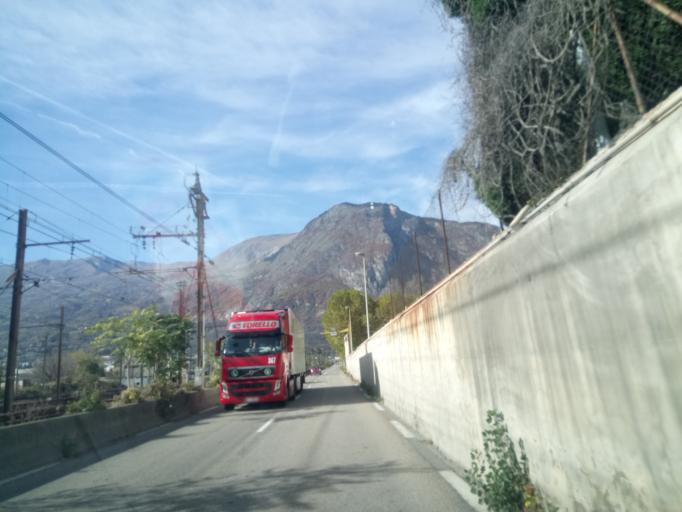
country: FR
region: Rhone-Alpes
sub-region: Departement de la Savoie
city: Villargondran
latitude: 45.2720
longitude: 6.3671
